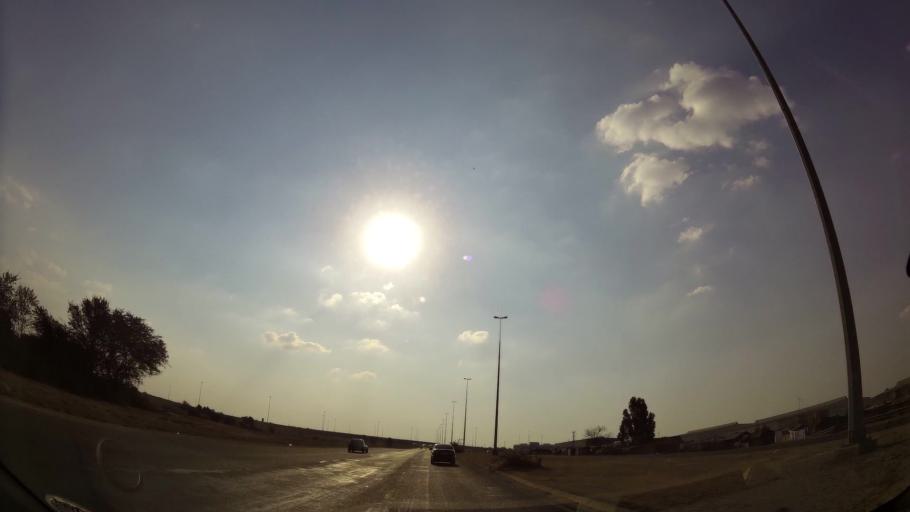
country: ZA
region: Gauteng
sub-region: City of Johannesburg Metropolitan Municipality
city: Modderfontein
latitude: -26.1073
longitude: 28.2585
